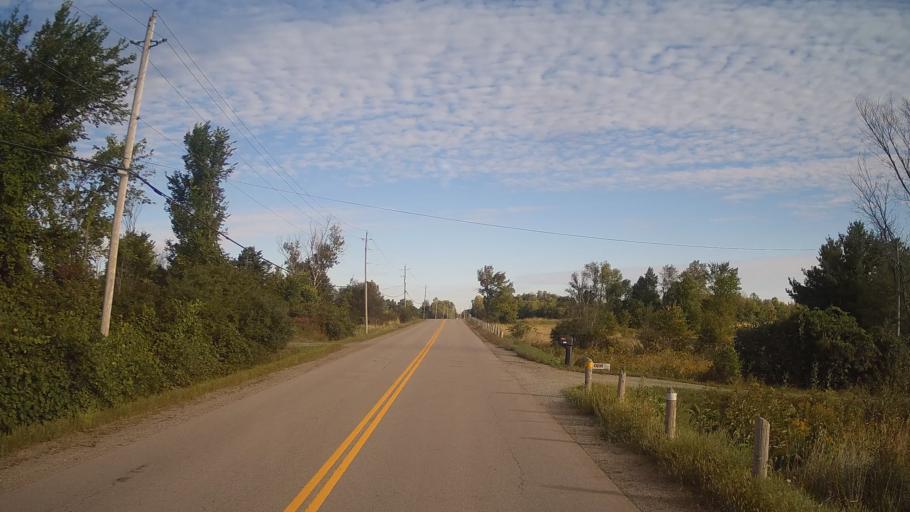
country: CA
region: Ontario
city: Gananoque
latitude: 44.3603
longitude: -76.1342
